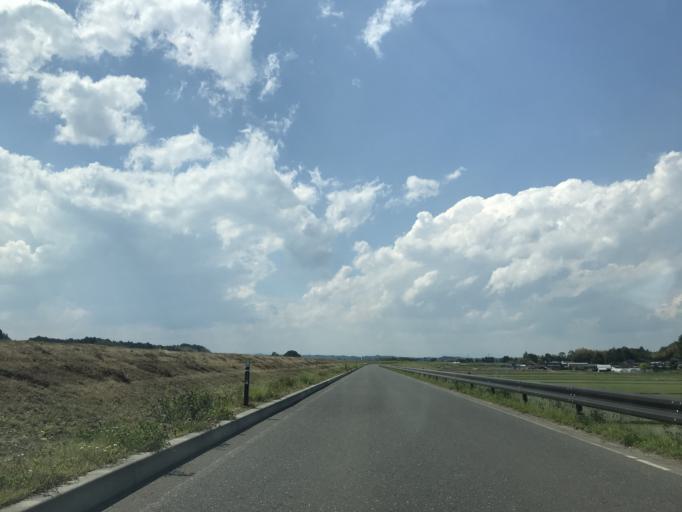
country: JP
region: Miyagi
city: Matsushima
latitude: 38.4330
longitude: 141.1218
